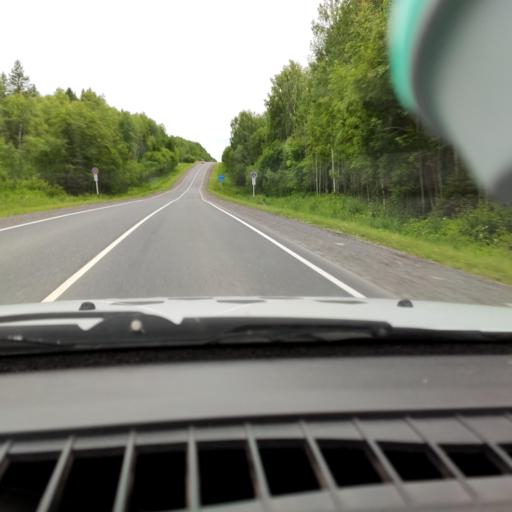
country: RU
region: Perm
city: Chusovoy
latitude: 58.2171
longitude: 57.8224
